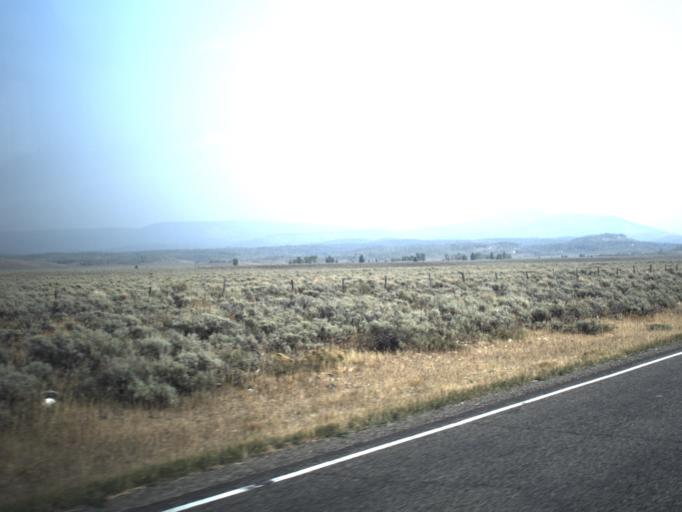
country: US
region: Wyoming
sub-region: Uinta County
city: Evanston
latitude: 40.9575
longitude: -110.8436
